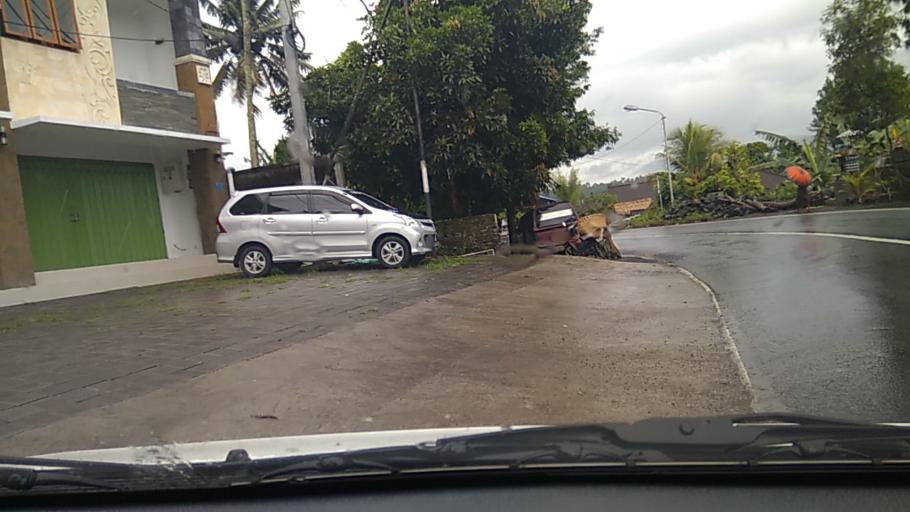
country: ID
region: Bali
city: Banjar Ababi
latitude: -8.4207
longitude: 115.5919
